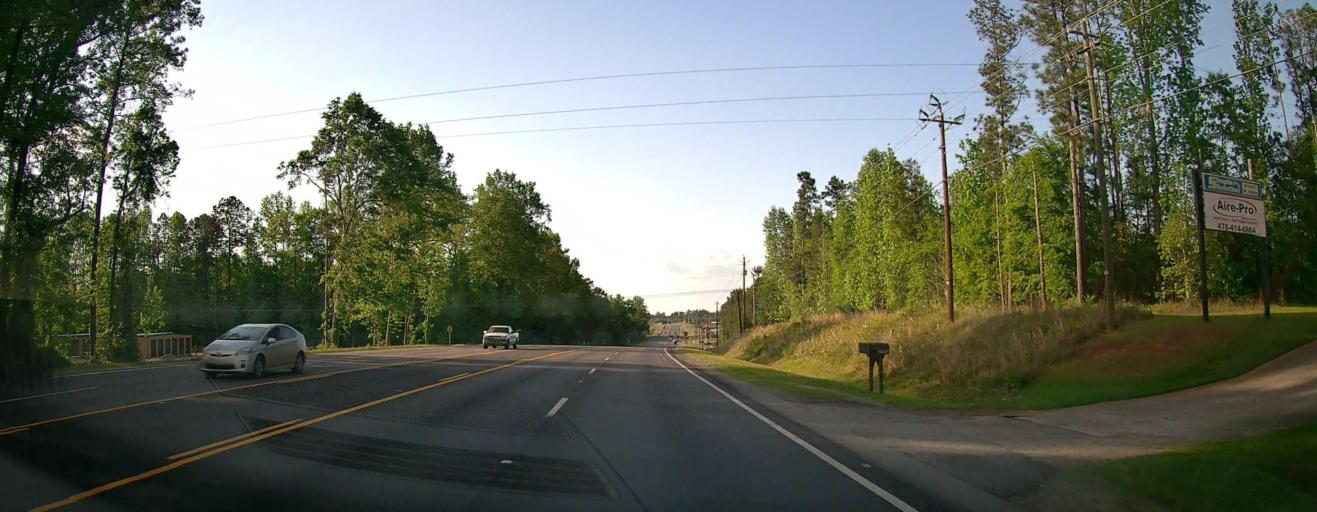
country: US
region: Georgia
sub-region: Baldwin County
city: Milledgeville
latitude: 33.1451
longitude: -83.2723
